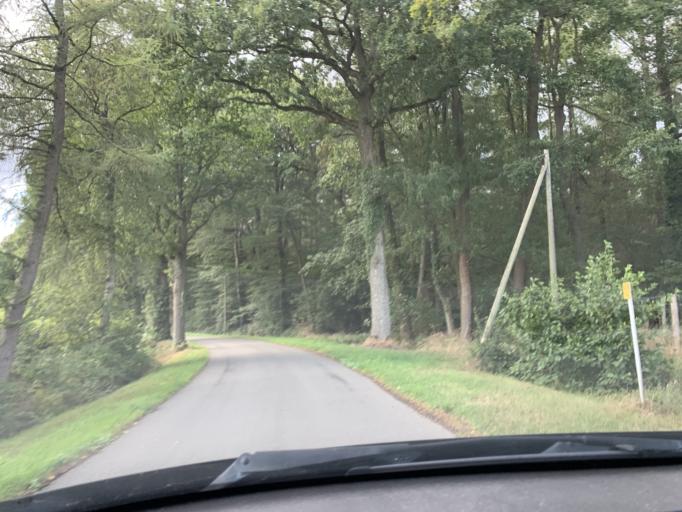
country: DE
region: Lower Saxony
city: Bad Zwischenahn
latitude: 53.2614
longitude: 8.0124
